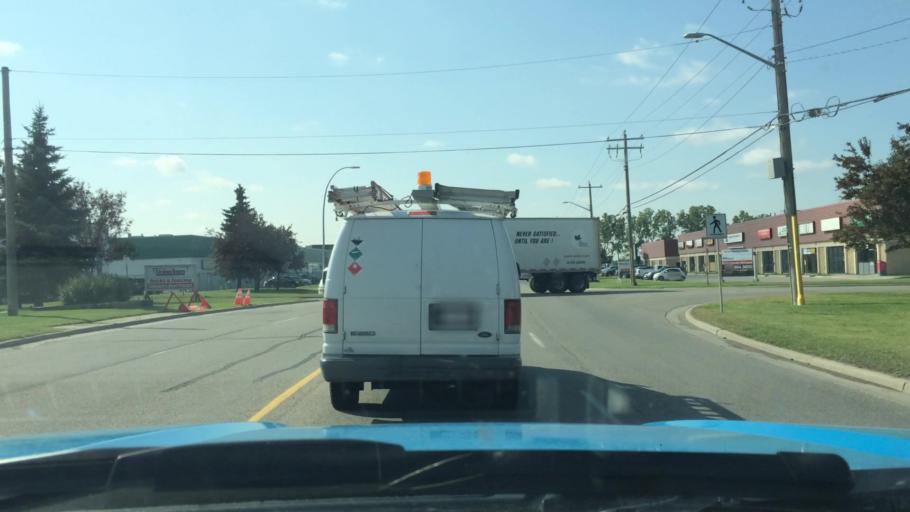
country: CA
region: Alberta
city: Calgary
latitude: 51.0840
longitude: -114.0297
